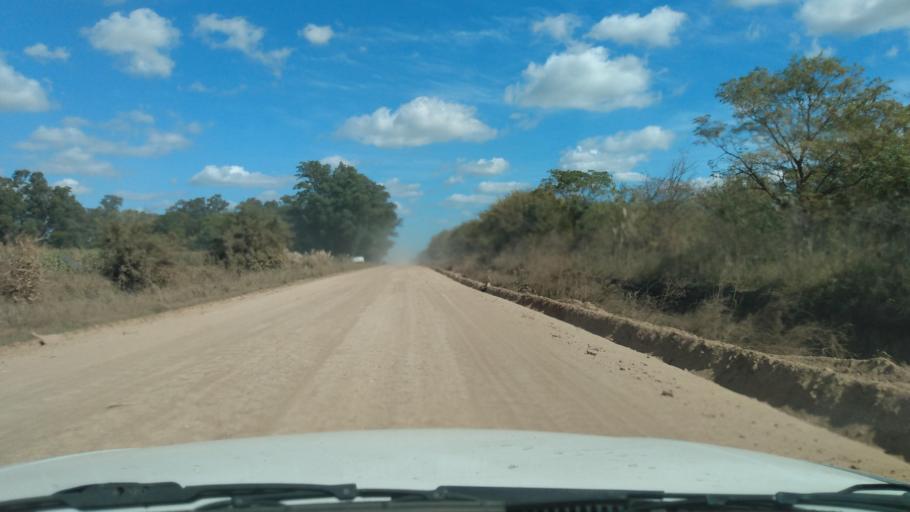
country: AR
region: Buenos Aires
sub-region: Partido de Navarro
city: Navarro
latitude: -35.0235
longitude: -59.4360
